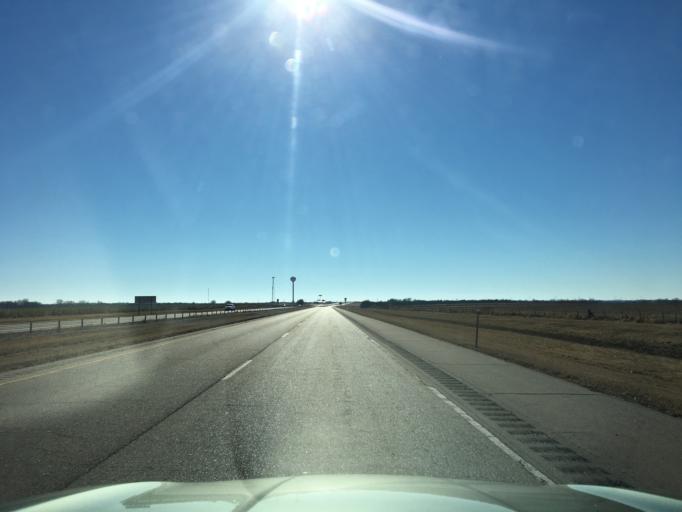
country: US
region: Oklahoma
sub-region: Kay County
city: Blackwell
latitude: 36.9534
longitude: -97.3458
